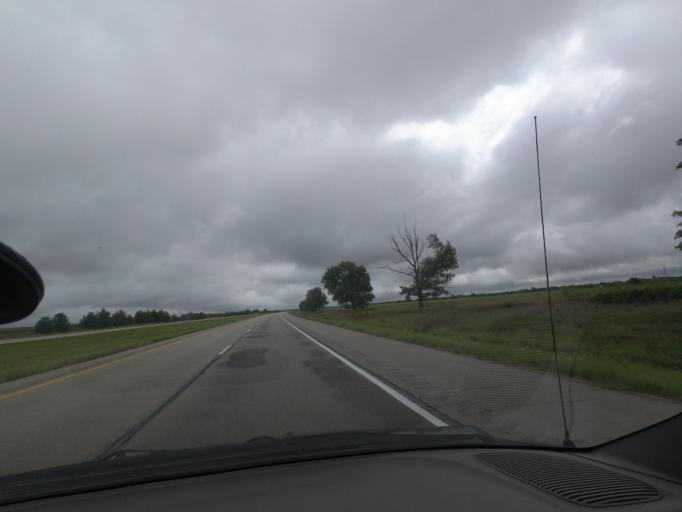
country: US
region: Illinois
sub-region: Piatt County
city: Monticello
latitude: 40.0304
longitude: -88.6444
